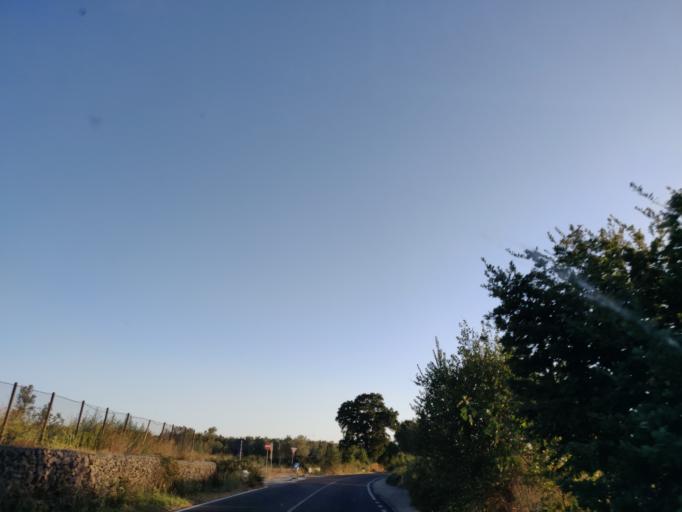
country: IT
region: Latium
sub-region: Provincia di Viterbo
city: Canino
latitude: 42.4266
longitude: 11.7111
